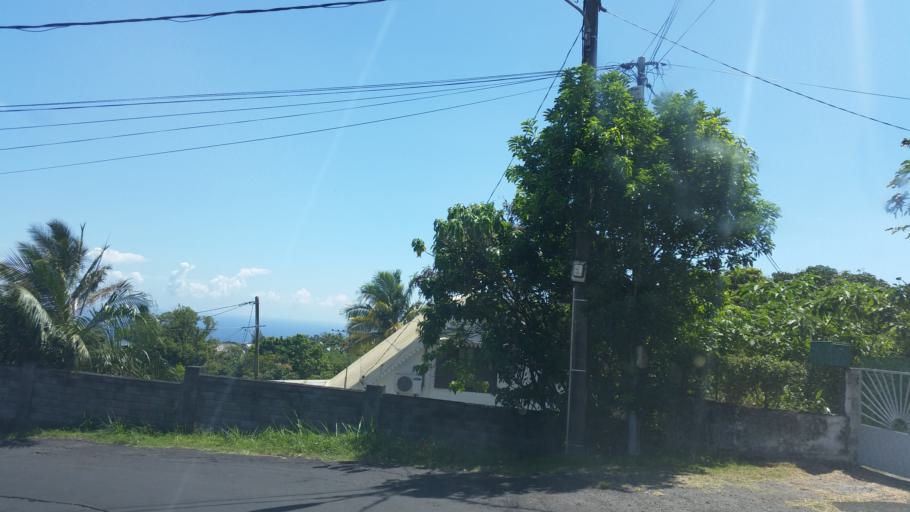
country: RE
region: Reunion
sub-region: Reunion
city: Sainte-Marie
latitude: -20.9356
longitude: 55.5293
